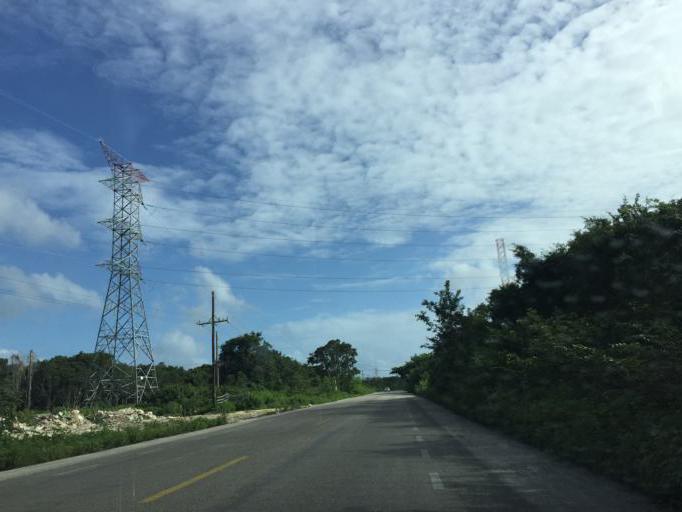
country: MX
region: Quintana Roo
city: Tulum
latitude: 20.2607
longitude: -87.4720
